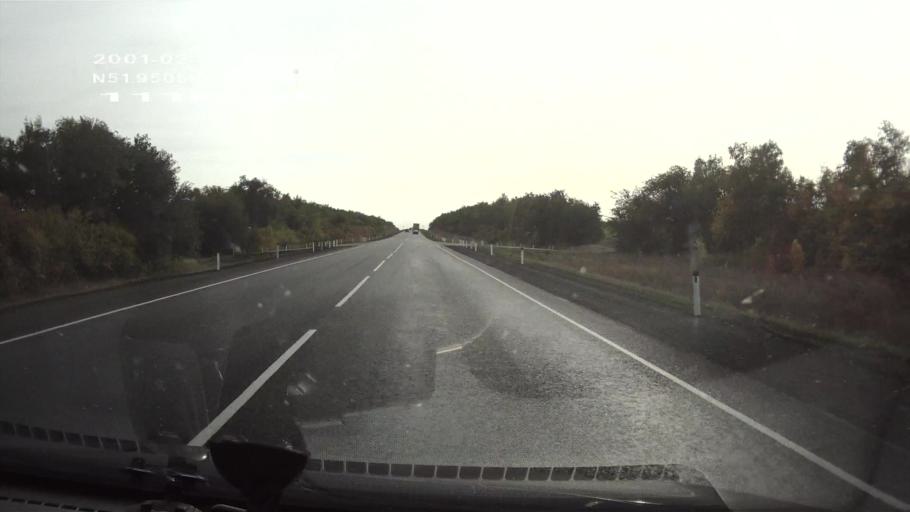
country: RU
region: Saratov
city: Sinodskoye
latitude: 51.9502
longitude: 46.6074
